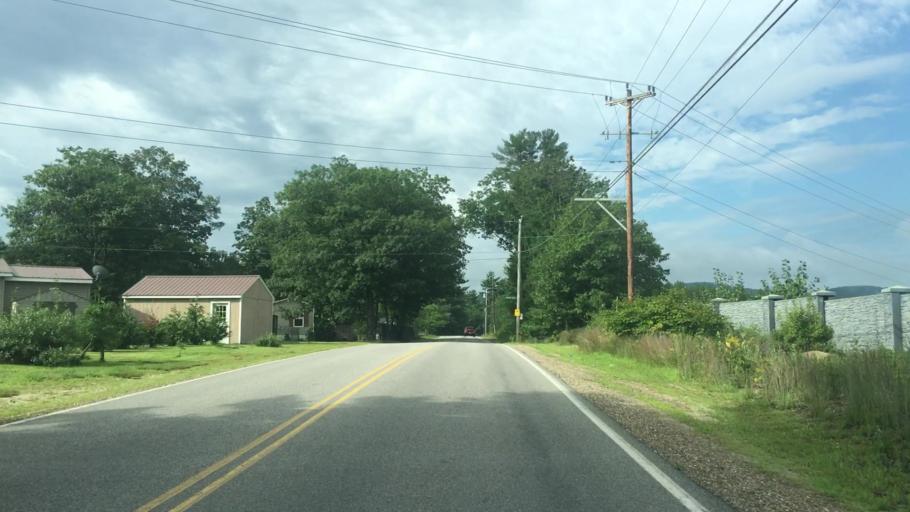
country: US
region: New Hampshire
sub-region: Strafford County
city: Farmington
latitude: 43.3790
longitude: -71.0373
